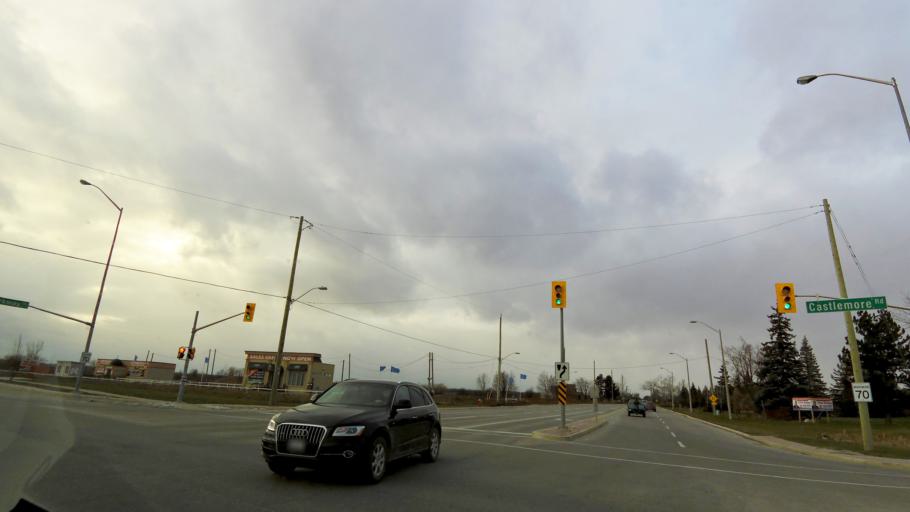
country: CA
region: Ontario
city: Brampton
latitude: 43.8011
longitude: -79.6786
